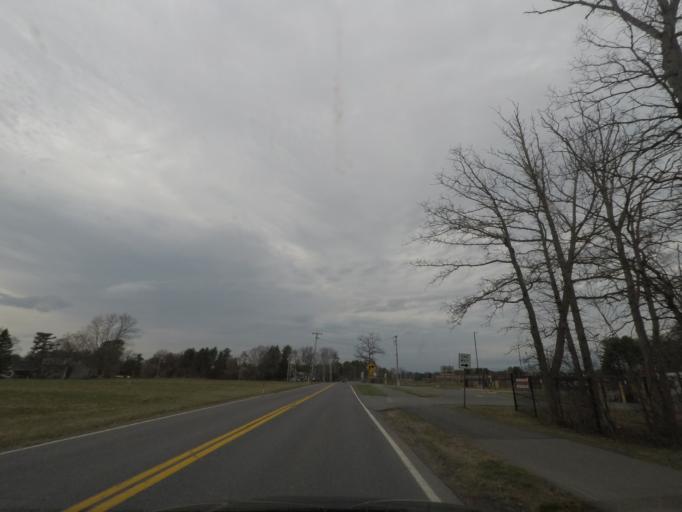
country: US
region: New York
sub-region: Albany County
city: Delmar
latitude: 42.6074
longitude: -73.8562
